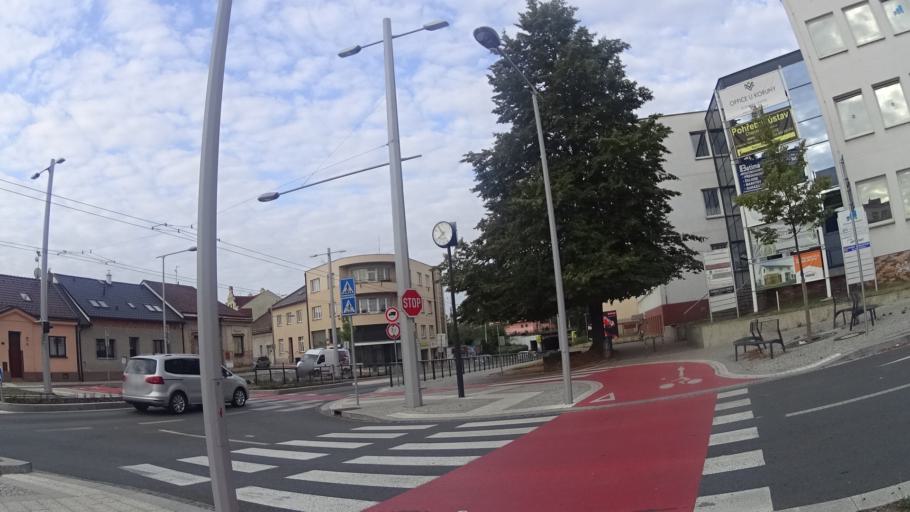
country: CZ
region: Kralovehradecky
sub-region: Okres Hradec Kralove
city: Hradec Kralove
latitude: 50.2116
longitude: 15.8108
